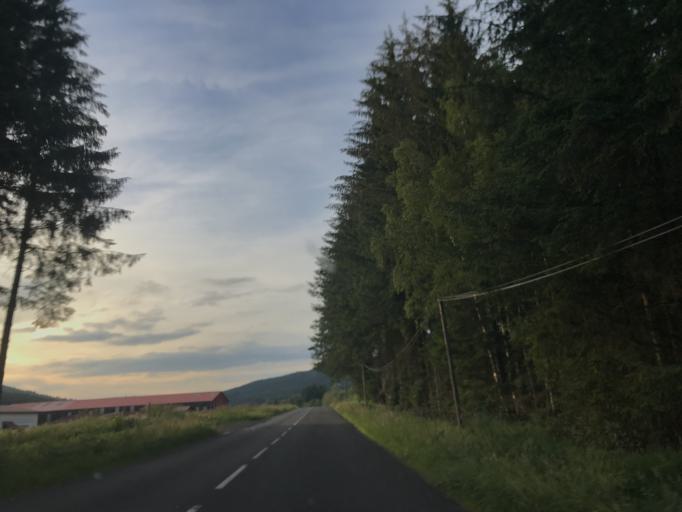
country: FR
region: Rhone-Alpes
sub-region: Departement de la Loire
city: Noiretable
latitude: 45.7748
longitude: 3.6799
